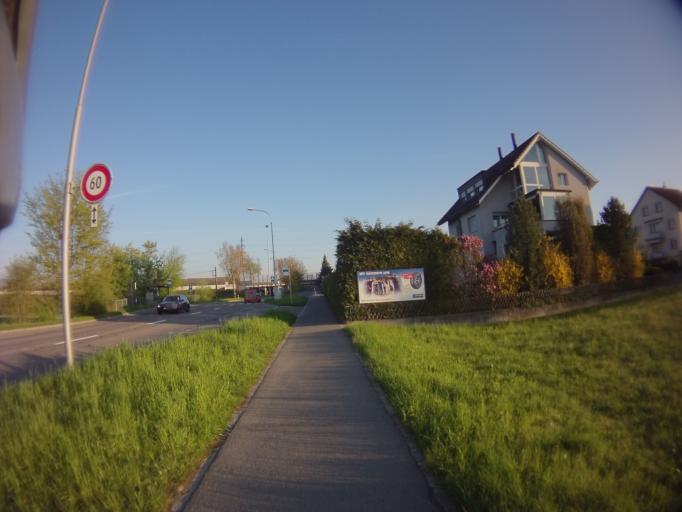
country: CH
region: Zug
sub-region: Zug
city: Cham
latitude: 47.1935
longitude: 8.4552
